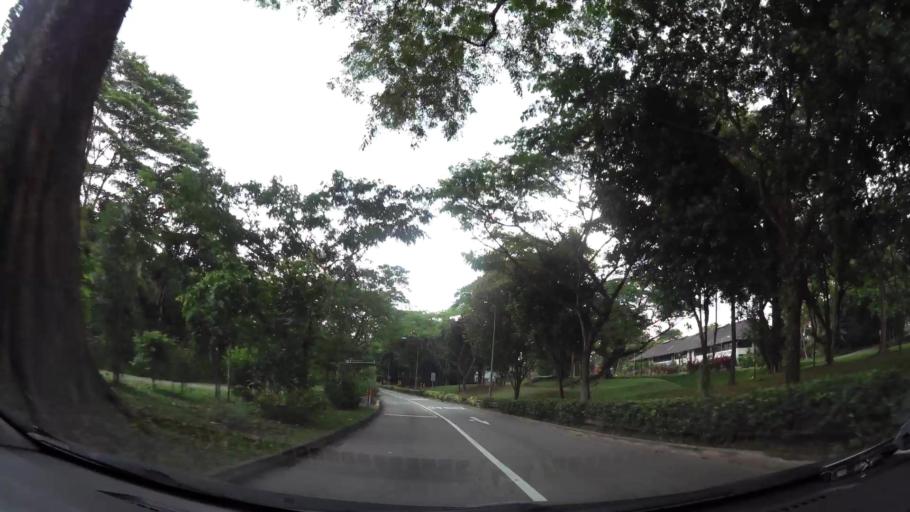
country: MY
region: Johor
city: Kampung Pasir Gudang Baru
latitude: 1.4561
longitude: 103.8345
